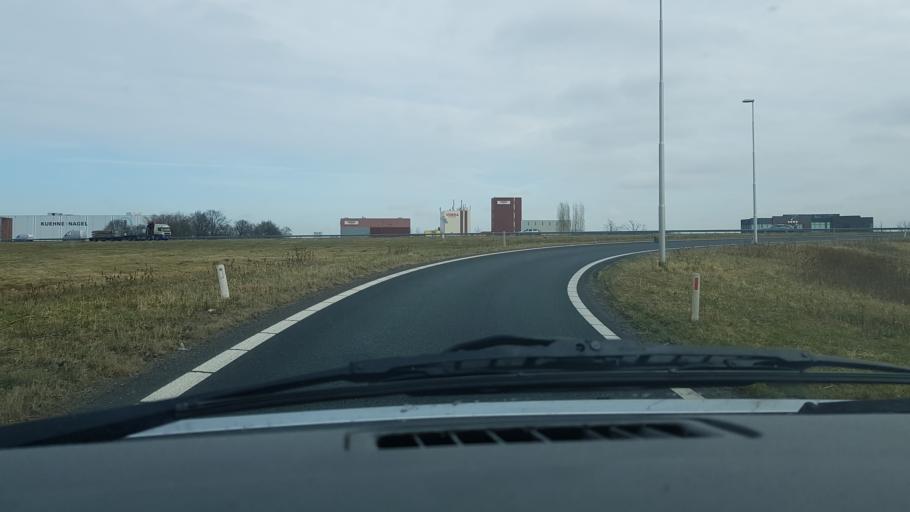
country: NL
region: North Brabant
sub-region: Gemeente Veghel
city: Eerde
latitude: 51.6041
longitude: 5.5090
